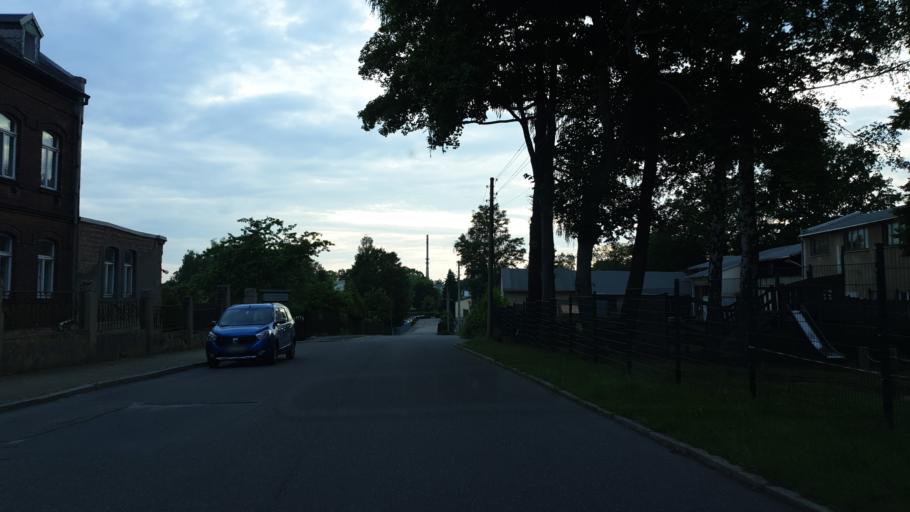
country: DE
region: Saxony
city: Hohenstein-Ernstthal
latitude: 50.7959
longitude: 12.7103
